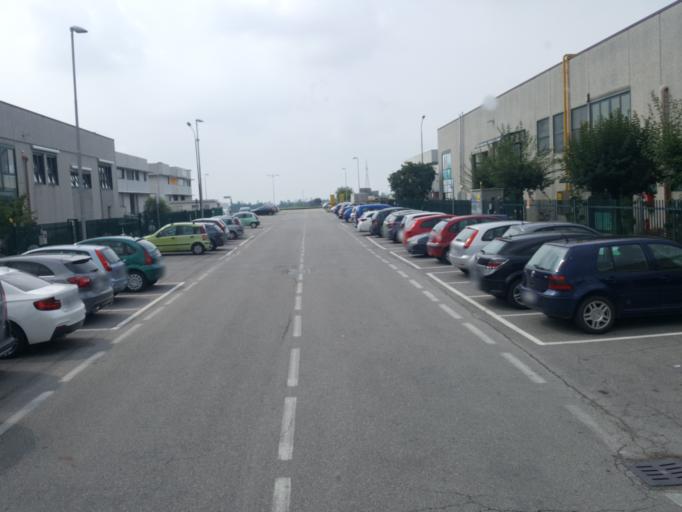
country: IT
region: Lombardy
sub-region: Provincia di Bergamo
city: Grassobbio
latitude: 45.6499
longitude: 9.7133
